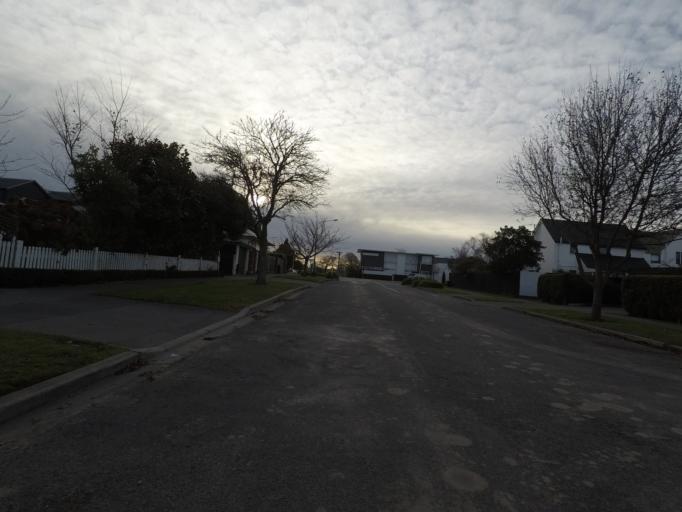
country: NZ
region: Canterbury
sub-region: Christchurch City
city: Christchurch
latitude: -43.5184
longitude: 172.6191
